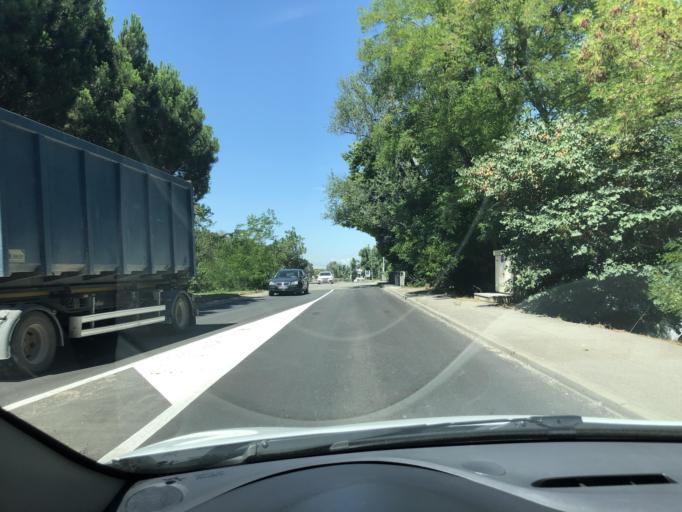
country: FR
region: Provence-Alpes-Cote d'Azur
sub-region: Departement des Bouches-du-Rhone
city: Noves
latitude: 43.8897
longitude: 4.8802
